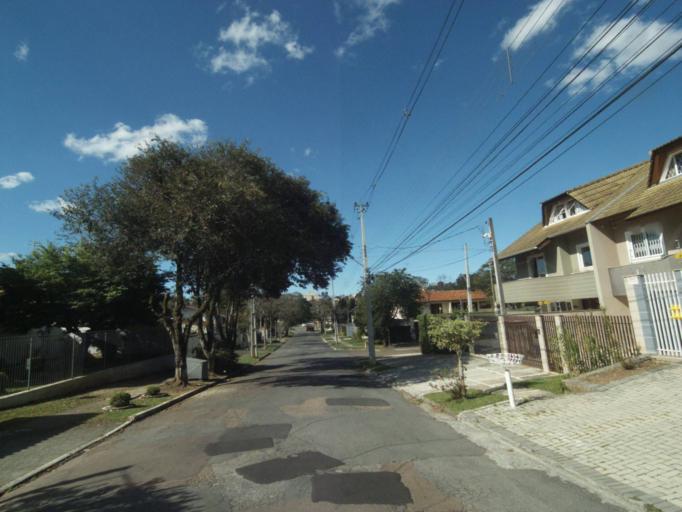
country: BR
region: Parana
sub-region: Curitiba
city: Curitiba
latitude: -25.3862
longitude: -49.2429
